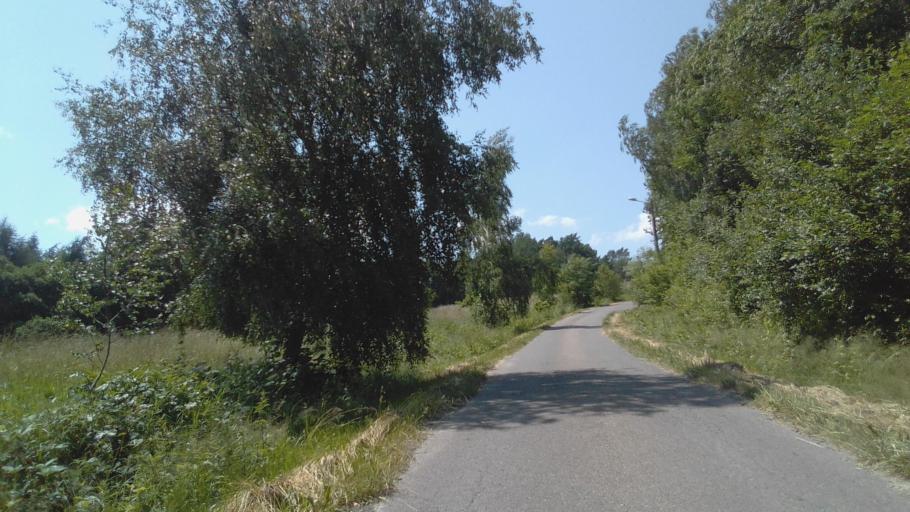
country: PL
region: Subcarpathian Voivodeship
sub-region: Powiat strzyzowski
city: Strzyzow
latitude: 49.8621
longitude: 21.7652
